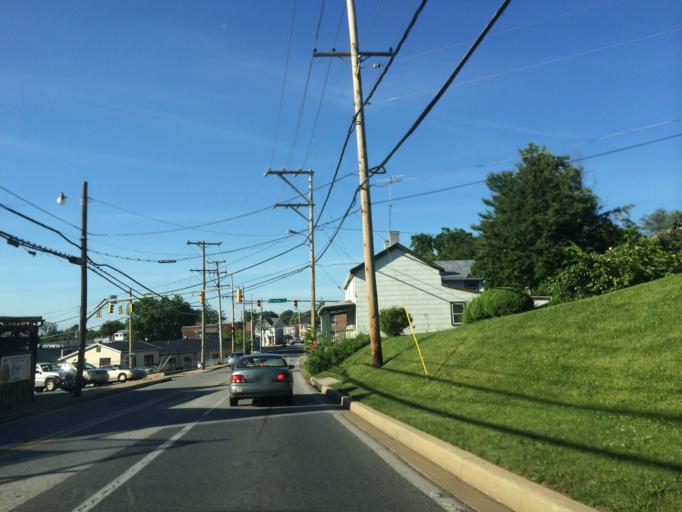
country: US
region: Maryland
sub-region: Carroll County
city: Westminster
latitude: 39.5648
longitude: -76.9882
